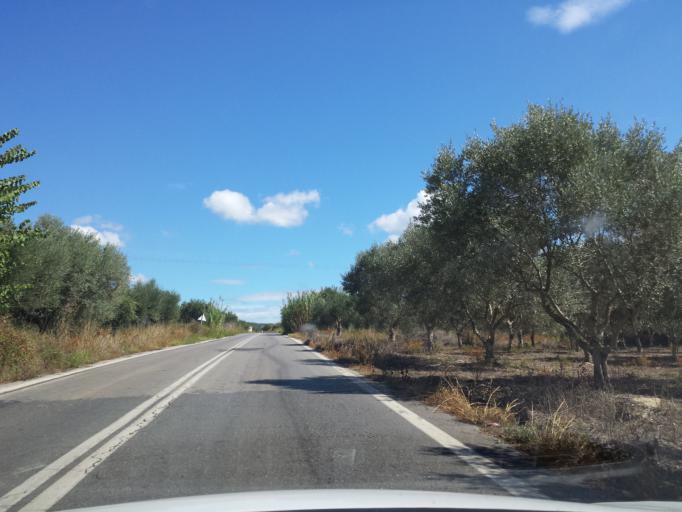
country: GR
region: Peloponnese
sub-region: Nomos Messinias
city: Pylos
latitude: 36.9530
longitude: 21.7636
